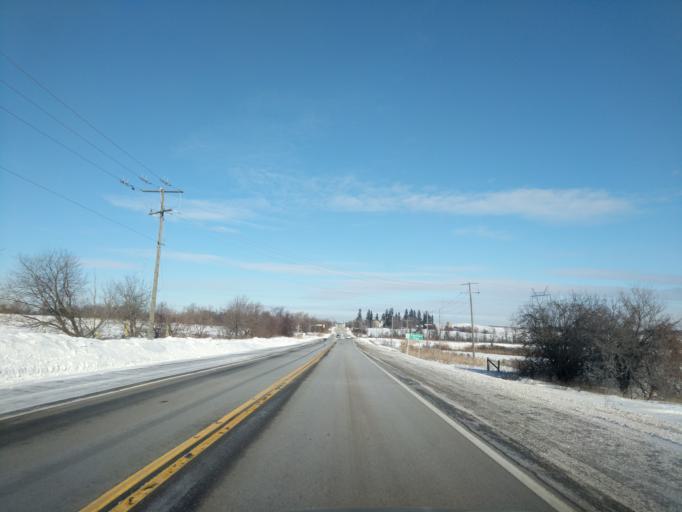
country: CA
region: Ontario
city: Pickering
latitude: 43.8568
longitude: -79.1536
